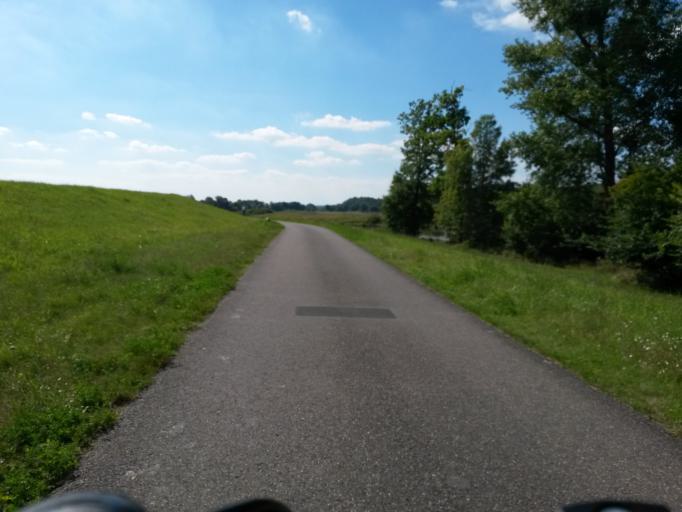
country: DE
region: Brandenburg
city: Meyenburg
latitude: 52.9976
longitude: 14.2054
